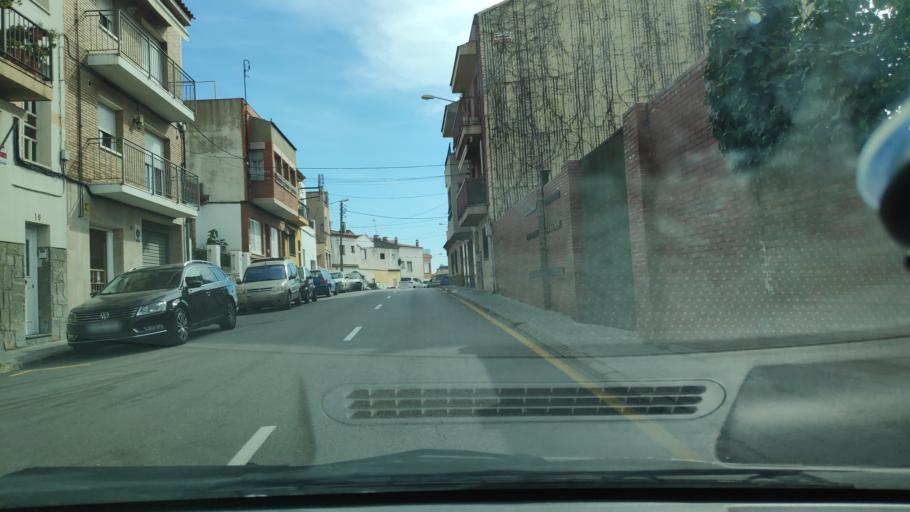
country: ES
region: Catalonia
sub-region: Provincia de Barcelona
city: Rubi
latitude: 41.4954
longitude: 2.0328
